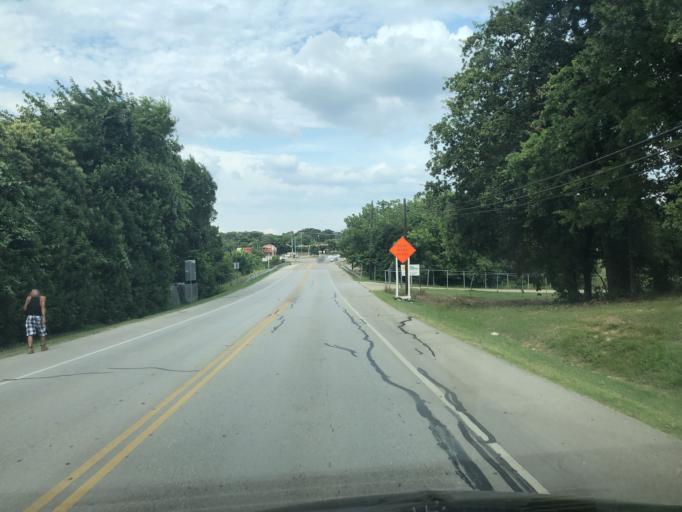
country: US
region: Texas
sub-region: Dallas County
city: Irving
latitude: 32.8050
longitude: -96.9972
